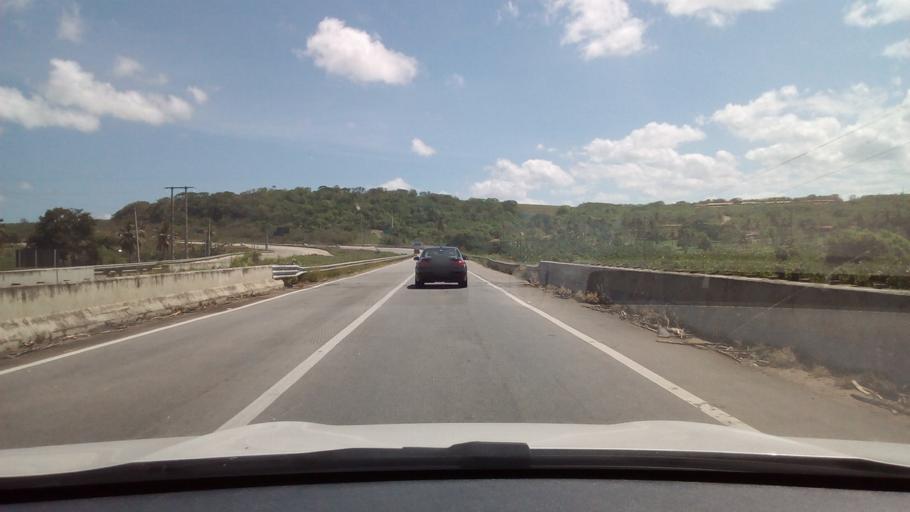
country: BR
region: Rio Grande do Norte
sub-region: Nisia Floresta
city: Nisia Floresta
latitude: -6.1116
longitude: -35.2337
